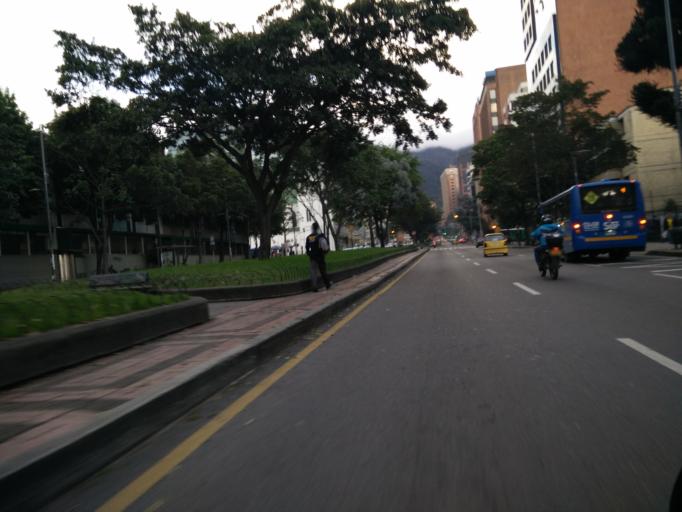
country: CO
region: Bogota D.C.
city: Barrio San Luis
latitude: 4.6577
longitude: -74.0597
